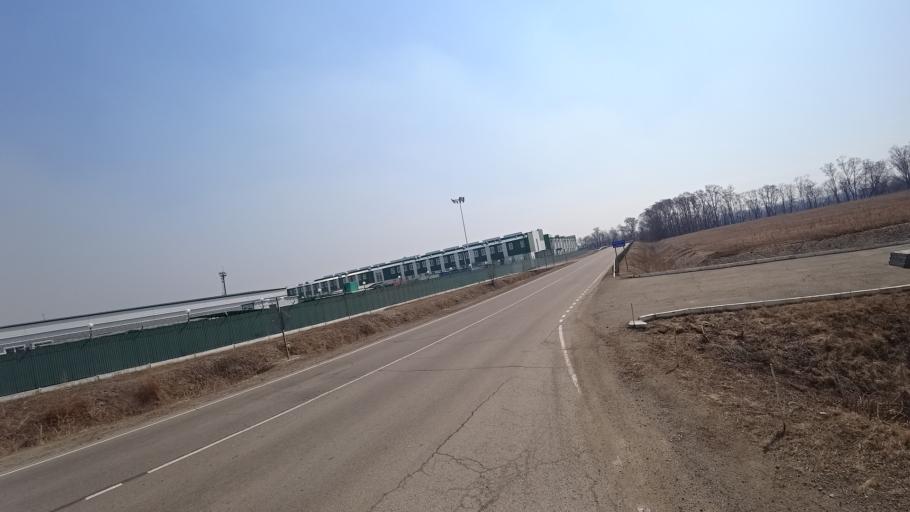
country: RU
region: Amur
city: Novobureyskiy
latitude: 49.7849
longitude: 129.9217
